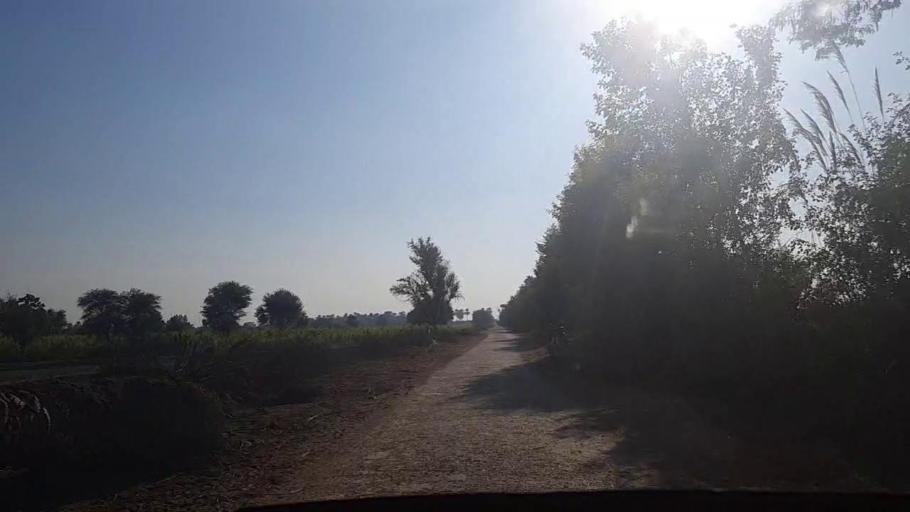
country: PK
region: Sindh
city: Gambat
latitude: 27.3596
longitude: 68.4568
